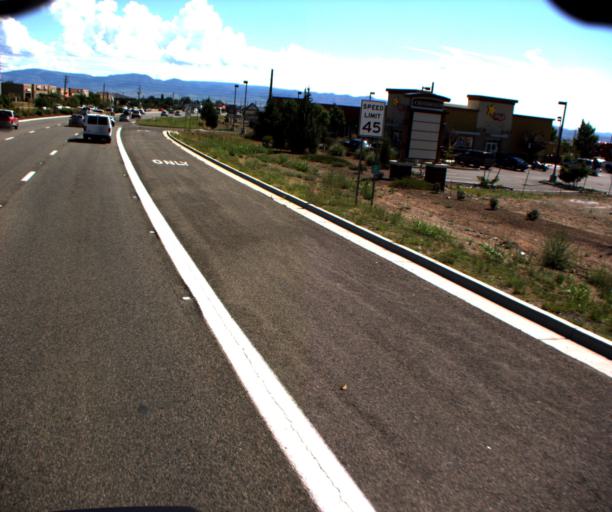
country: US
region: Arizona
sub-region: Yavapai County
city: Prescott Valley
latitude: 34.5777
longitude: -112.3639
